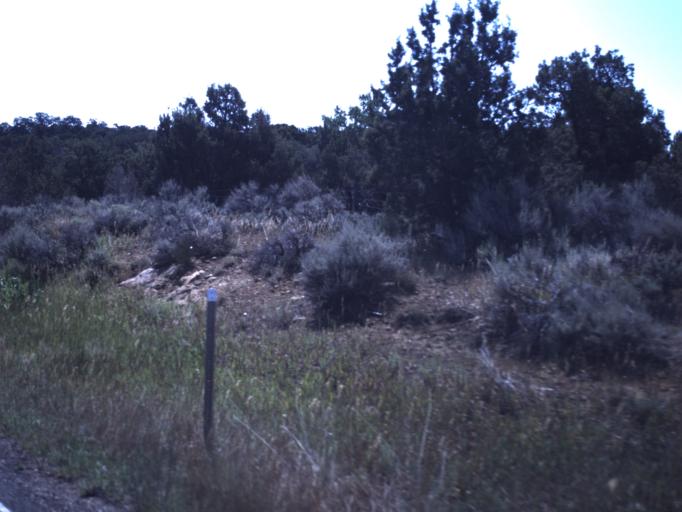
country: US
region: Utah
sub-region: Duchesne County
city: Duchesne
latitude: 40.3555
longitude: -110.3651
